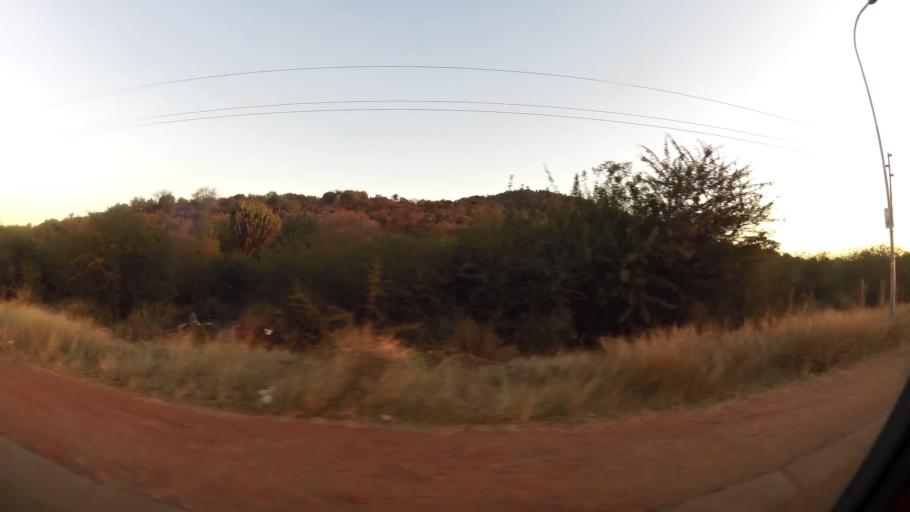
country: ZA
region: North-West
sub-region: Bojanala Platinum District Municipality
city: Rustenburg
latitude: -25.6086
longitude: 27.1865
